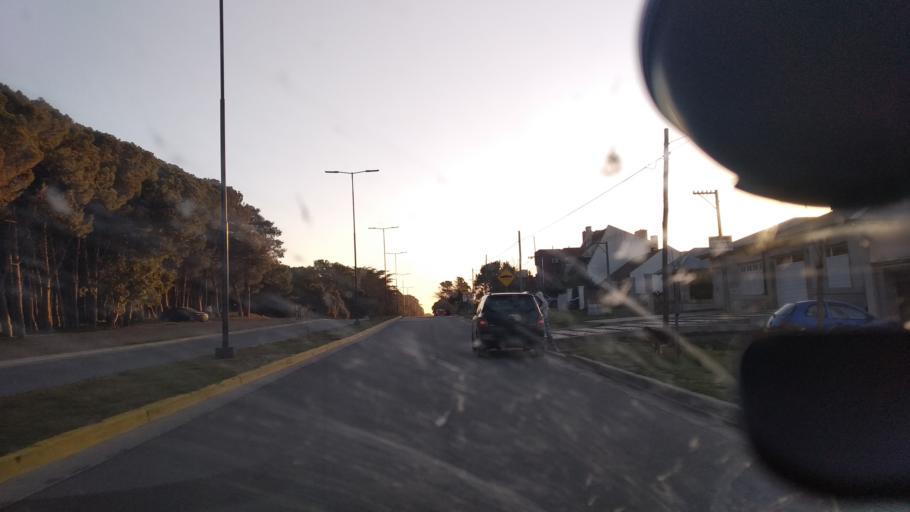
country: AR
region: Buenos Aires
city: Necochea
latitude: -38.5833
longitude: -58.7450
